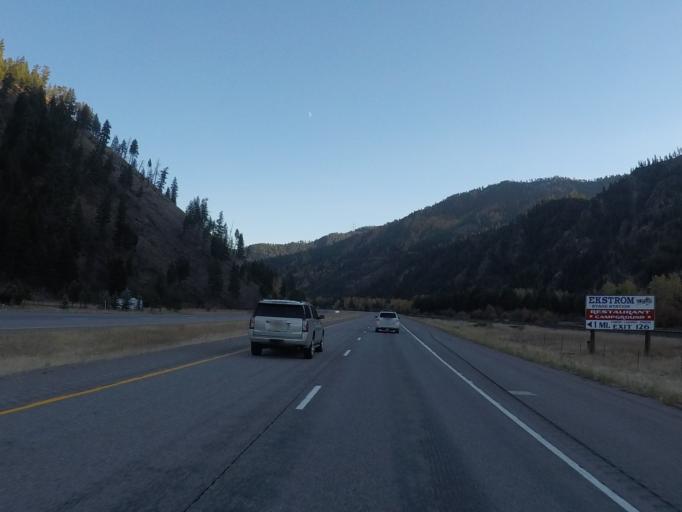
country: US
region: Montana
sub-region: Missoula County
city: Clinton
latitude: 46.7353
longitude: -113.6984
